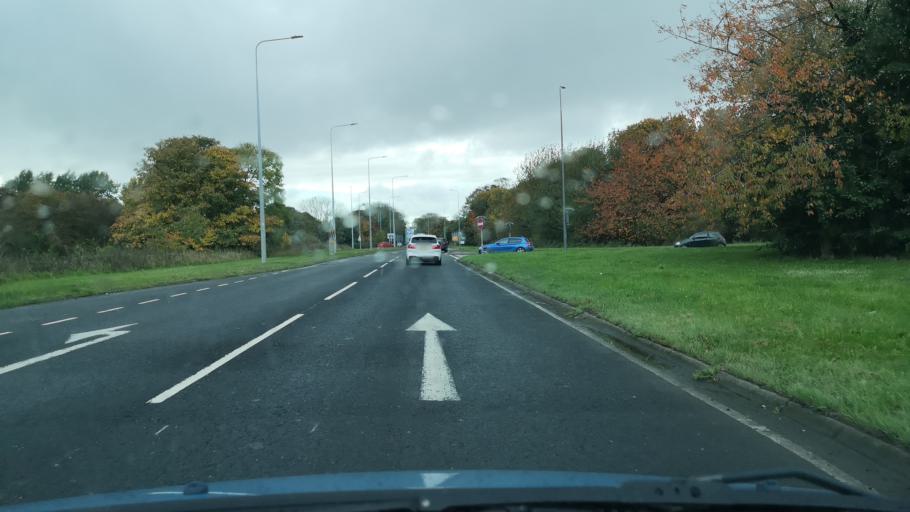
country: GB
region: England
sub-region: North Lincolnshire
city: Crowle
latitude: 53.5851
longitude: -0.8169
